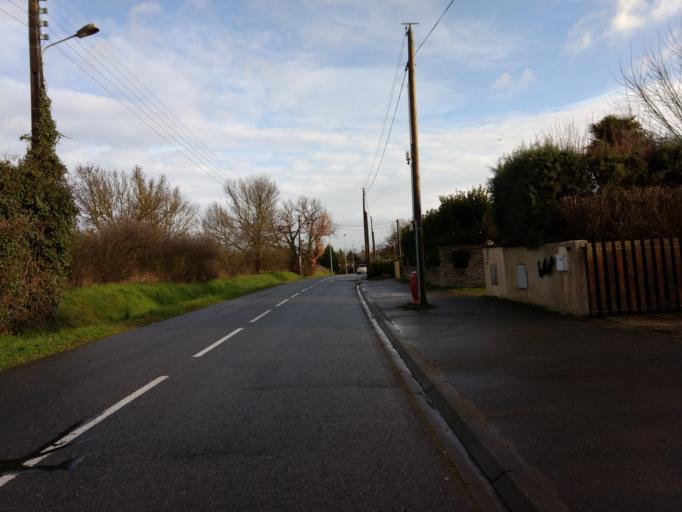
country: FR
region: Midi-Pyrenees
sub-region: Departement de la Haute-Garonne
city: Colomiers
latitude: 43.6107
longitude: 1.3173
